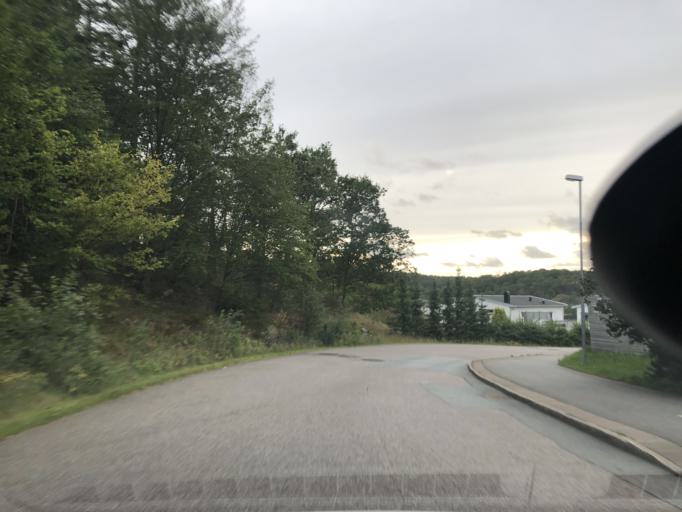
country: SE
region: Vaestra Goetaland
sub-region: Goteborg
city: Goeteborg
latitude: 57.7472
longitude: 11.9563
